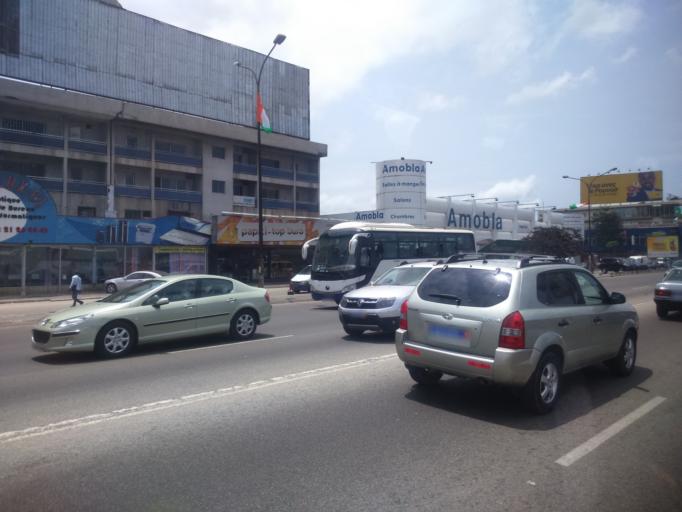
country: CI
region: Lagunes
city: Abidjan
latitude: 5.2988
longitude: -3.9865
